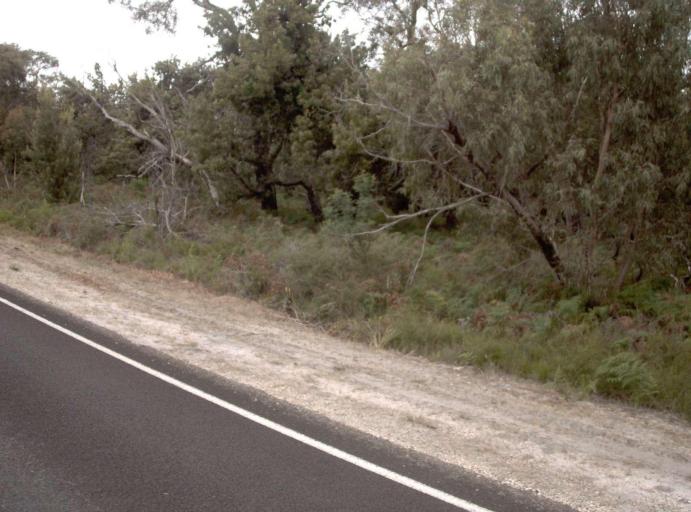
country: AU
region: Victoria
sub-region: East Gippsland
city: Bairnsdale
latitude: -38.0758
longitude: 147.5407
